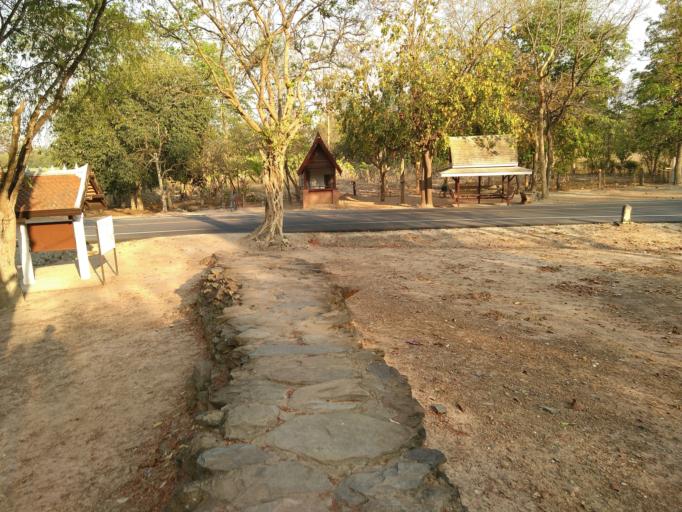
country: TH
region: Sukhothai
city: Ban Na
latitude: 17.0230
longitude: 99.6767
